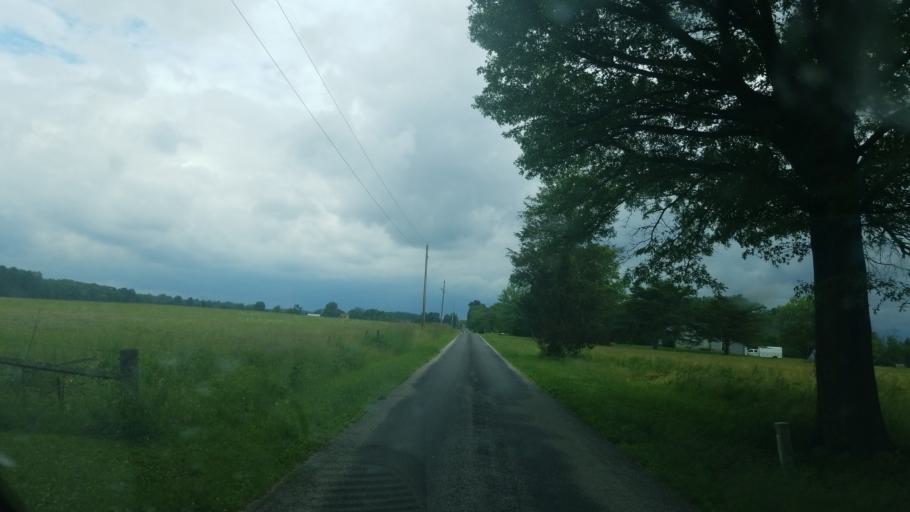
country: US
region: Ohio
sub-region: Morrow County
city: Cardington
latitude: 40.5506
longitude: -82.9670
